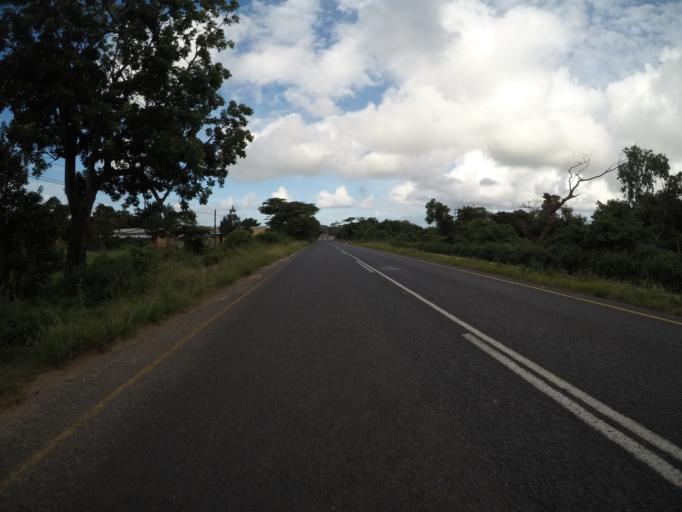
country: ZA
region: KwaZulu-Natal
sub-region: uMkhanyakude District Municipality
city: Mtubatuba
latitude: -28.3779
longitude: 32.3698
